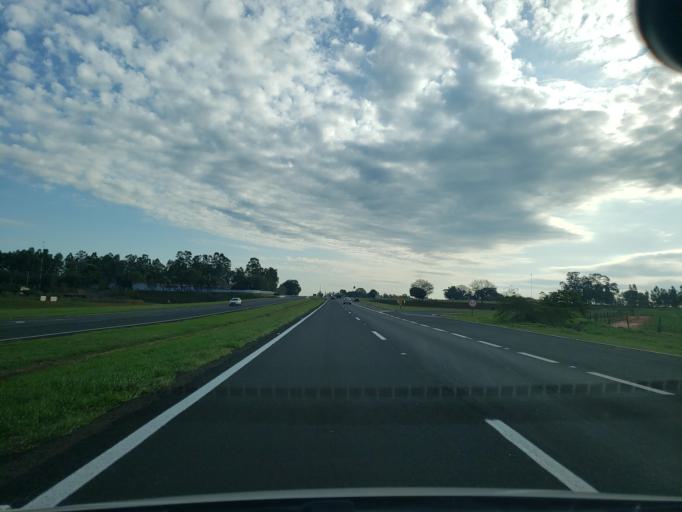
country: BR
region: Sao Paulo
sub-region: Guararapes
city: Guararapes
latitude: -21.2083
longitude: -50.6585
